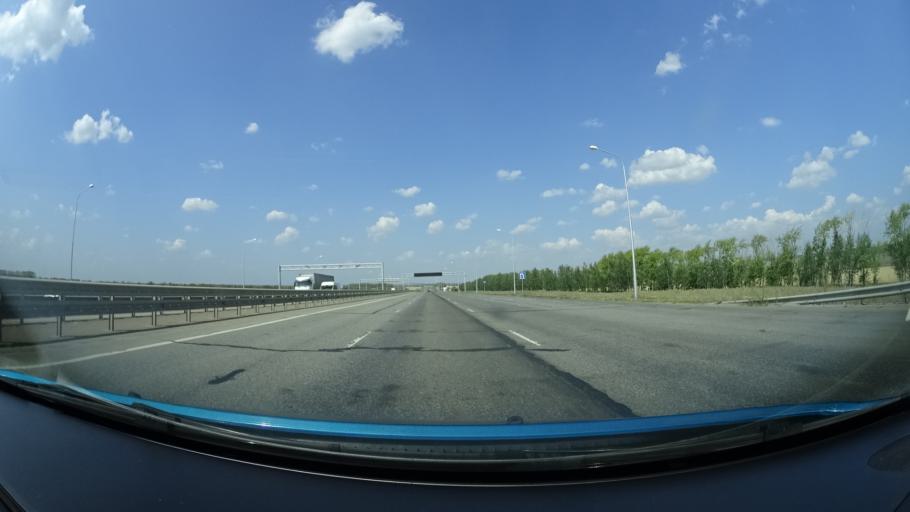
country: RU
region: Bashkortostan
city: Chishmy
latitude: 54.6697
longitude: 55.3941
